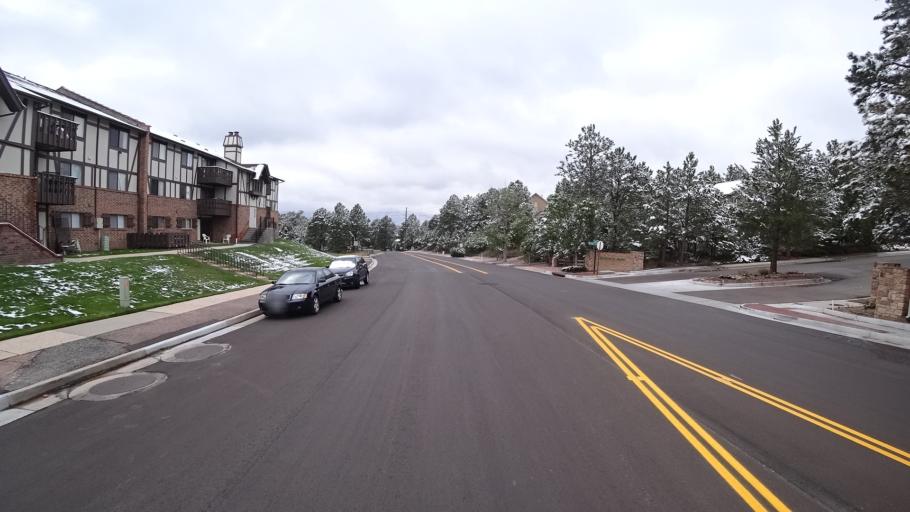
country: US
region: Colorado
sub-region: El Paso County
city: Colorado Springs
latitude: 38.9165
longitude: -104.7906
